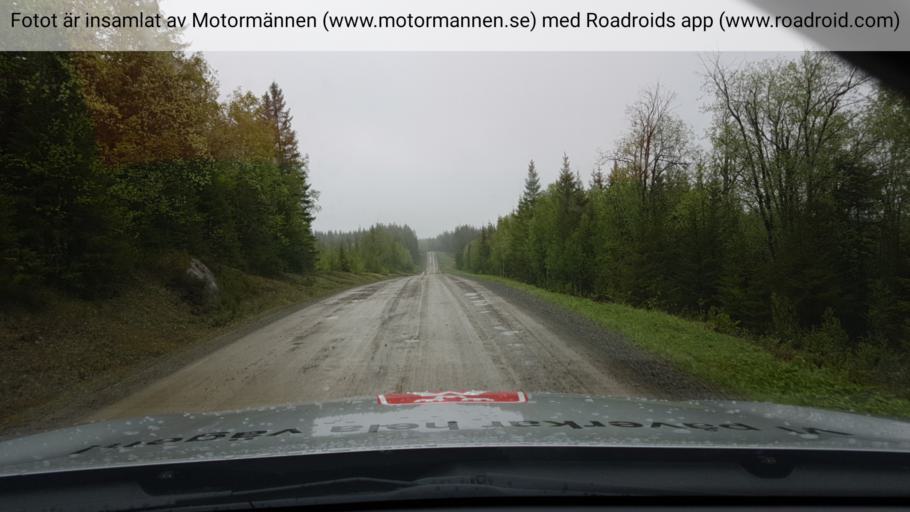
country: SE
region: Jaemtland
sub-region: Bergs Kommun
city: Hoverberg
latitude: 62.9942
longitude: 14.1575
